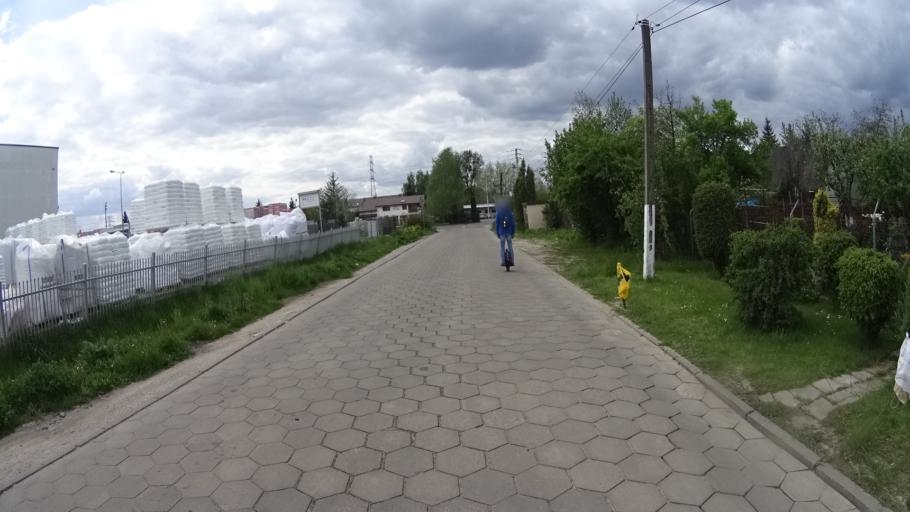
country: PL
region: Masovian Voivodeship
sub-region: Powiat warszawski zachodni
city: Babice
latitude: 52.2776
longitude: 20.8674
